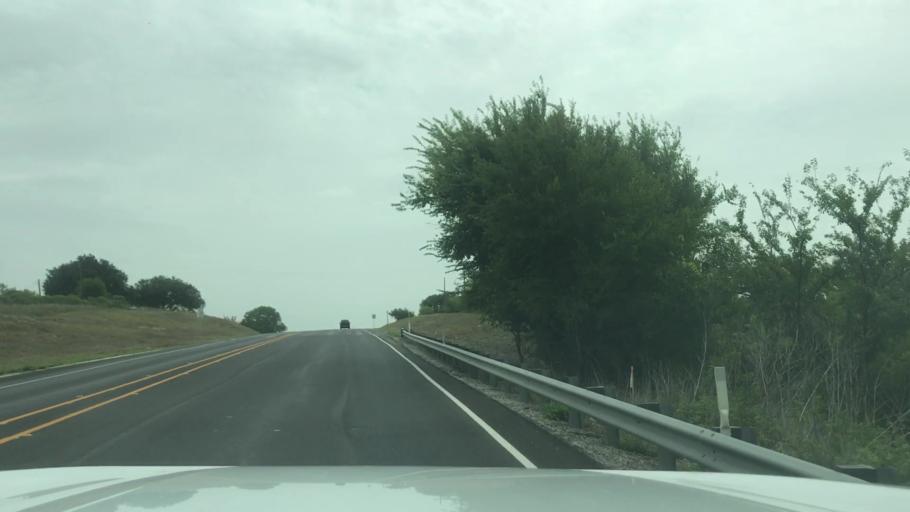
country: US
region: Texas
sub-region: Hamilton County
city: Hico
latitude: 31.9814
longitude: -98.0259
